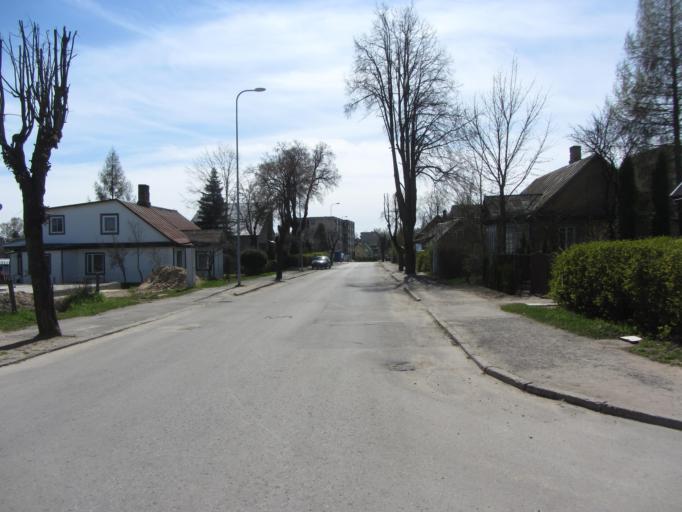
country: LT
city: Zarasai
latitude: 55.7380
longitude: 26.2467
